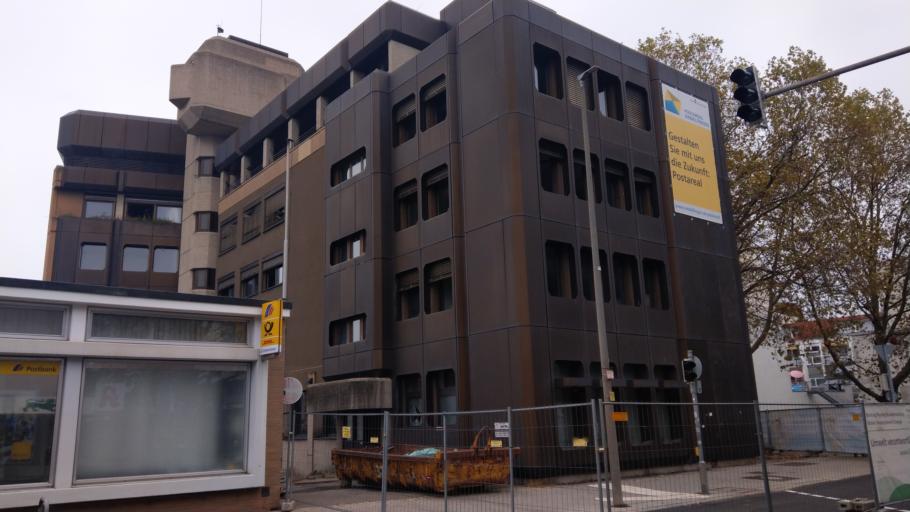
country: DE
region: Baden-Wuerttemberg
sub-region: Regierungsbezirk Stuttgart
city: Sindelfingen
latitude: 48.7073
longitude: 9.0006
